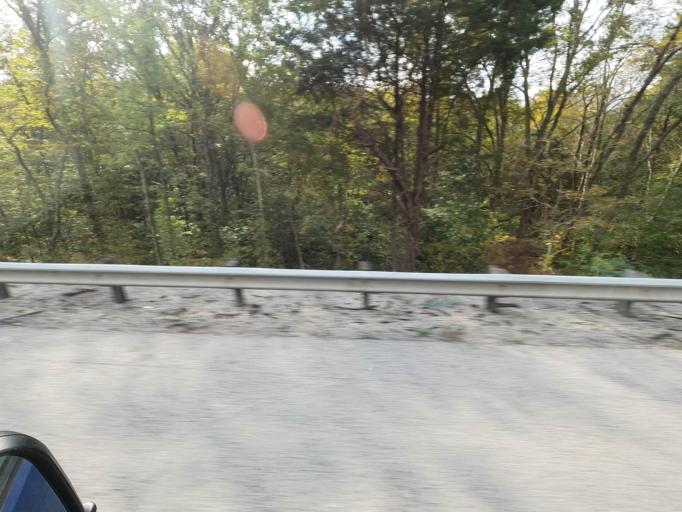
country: US
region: Tennessee
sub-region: Dickson County
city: Burns
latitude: 36.0175
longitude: -87.2513
